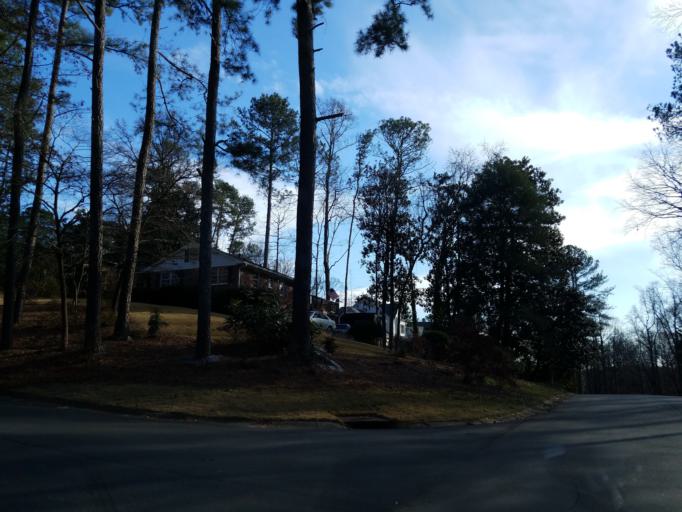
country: US
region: Georgia
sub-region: Cobb County
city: Vinings
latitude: 33.8565
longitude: -84.4876
